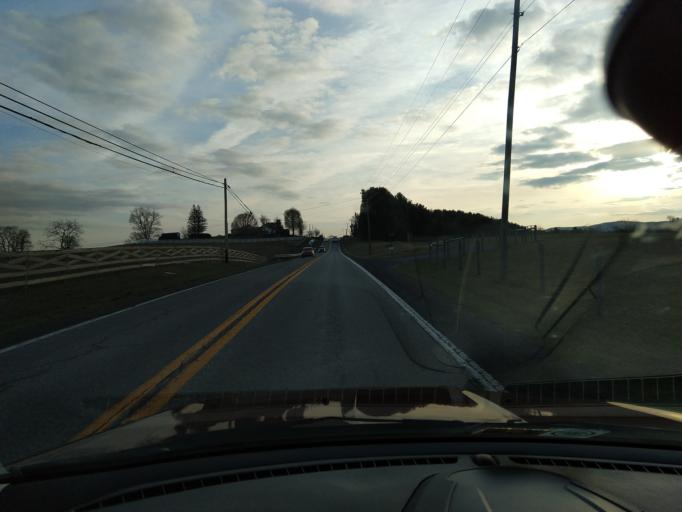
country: US
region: West Virginia
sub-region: Greenbrier County
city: Lewisburg
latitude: 37.9036
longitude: -80.3946
